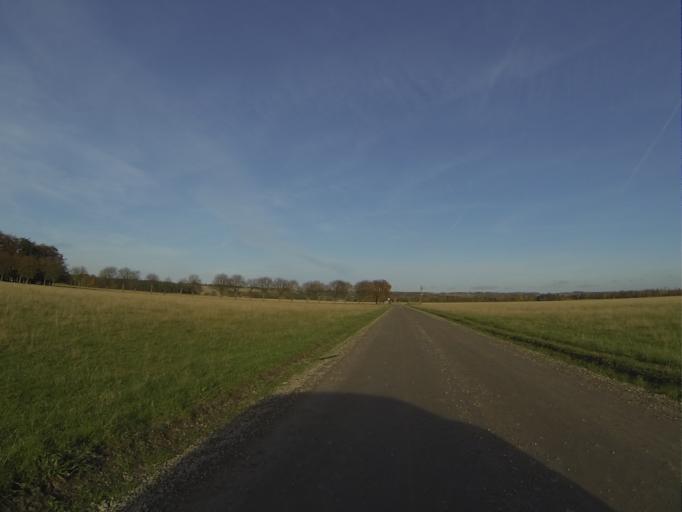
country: SE
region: Skane
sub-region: Hoors Kommun
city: Loberod
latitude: 55.7209
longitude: 13.4406
